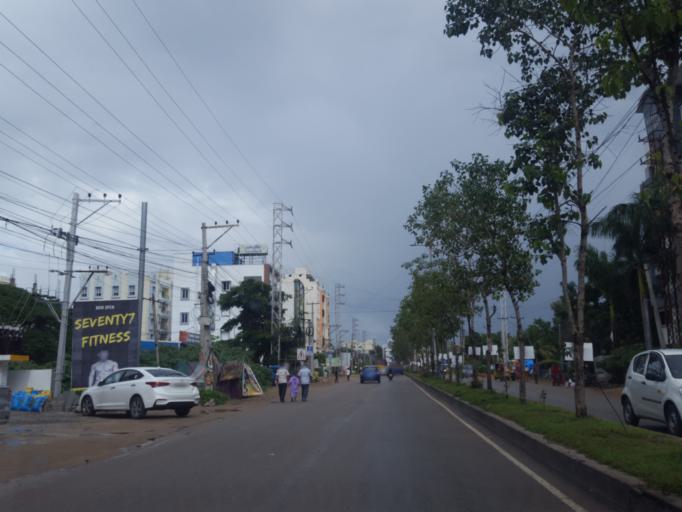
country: IN
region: Telangana
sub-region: Medak
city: Serilingampalle
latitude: 17.4798
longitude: 78.3164
